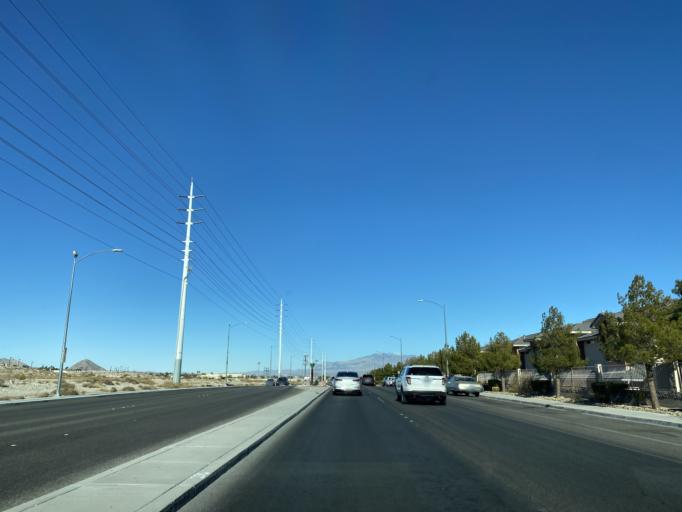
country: US
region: Nevada
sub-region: Clark County
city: Spring Valley
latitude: 36.1817
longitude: -115.2782
